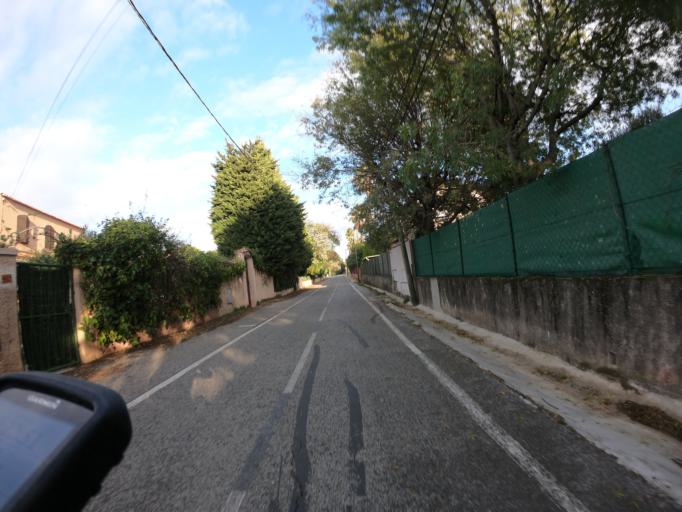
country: FR
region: Provence-Alpes-Cote d'Azur
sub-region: Departement du Var
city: La Garde
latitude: 43.1118
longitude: 5.9914
